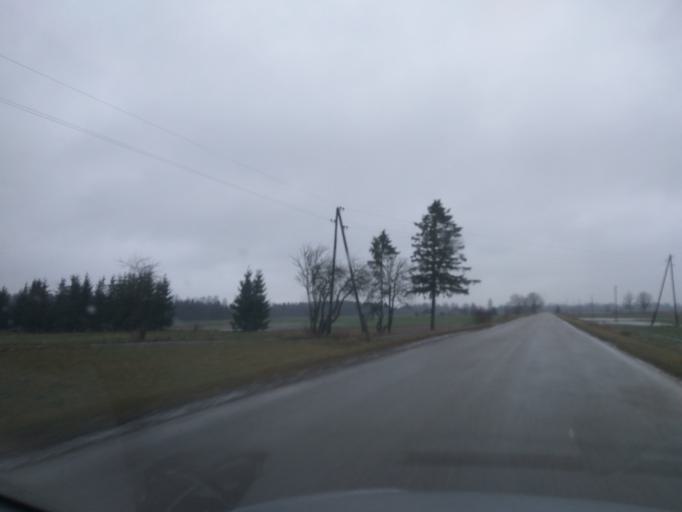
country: LV
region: Saldus Rajons
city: Saldus
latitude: 56.8391
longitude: 22.3789
